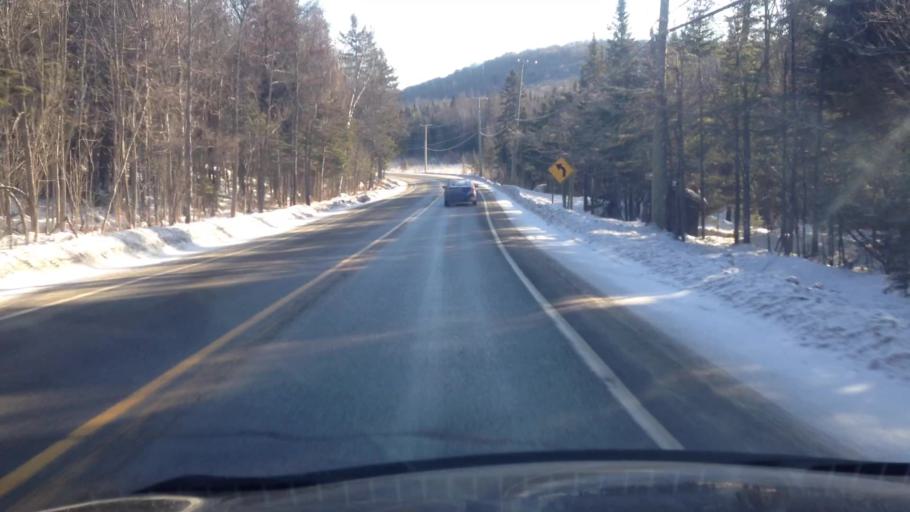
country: CA
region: Quebec
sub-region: Laurentides
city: Saint-Sauveur
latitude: 45.9090
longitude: -74.2857
